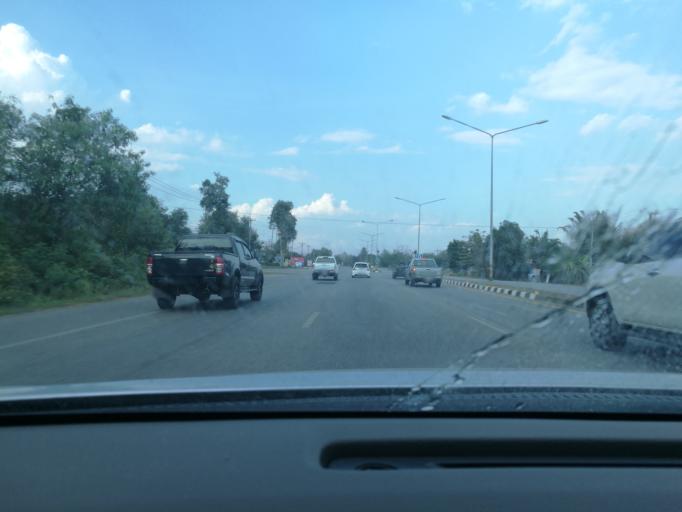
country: TH
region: Phetchabun
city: Phetchabun
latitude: 16.4810
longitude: 101.1593
